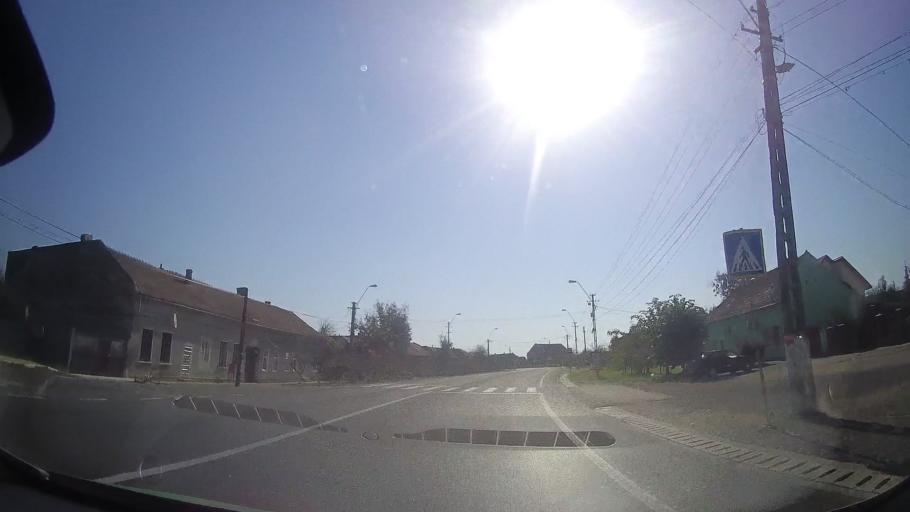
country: RO
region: Timis
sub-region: Comuna Belint
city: Belint
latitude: 45.7574
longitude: 21.7328
